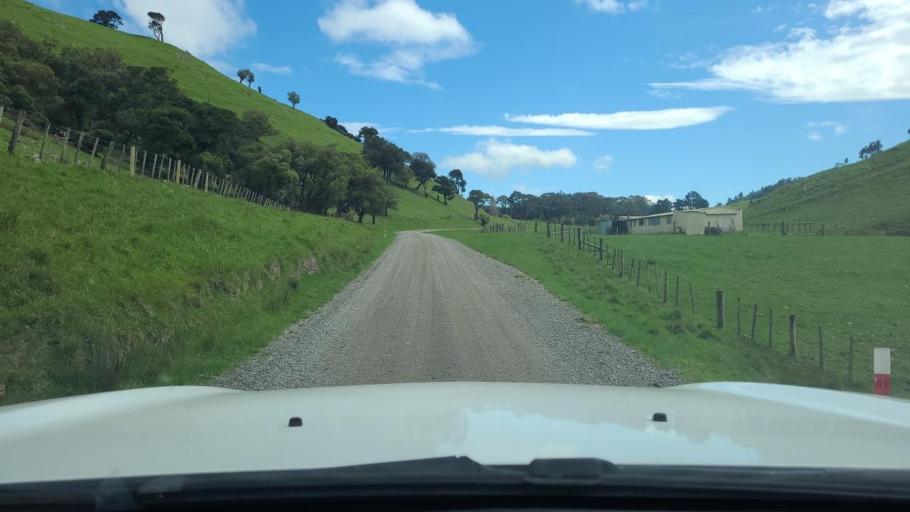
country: NZ
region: Wellington
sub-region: South Wairarapa District
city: Waipawa
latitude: -41.3236
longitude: 175.3847
